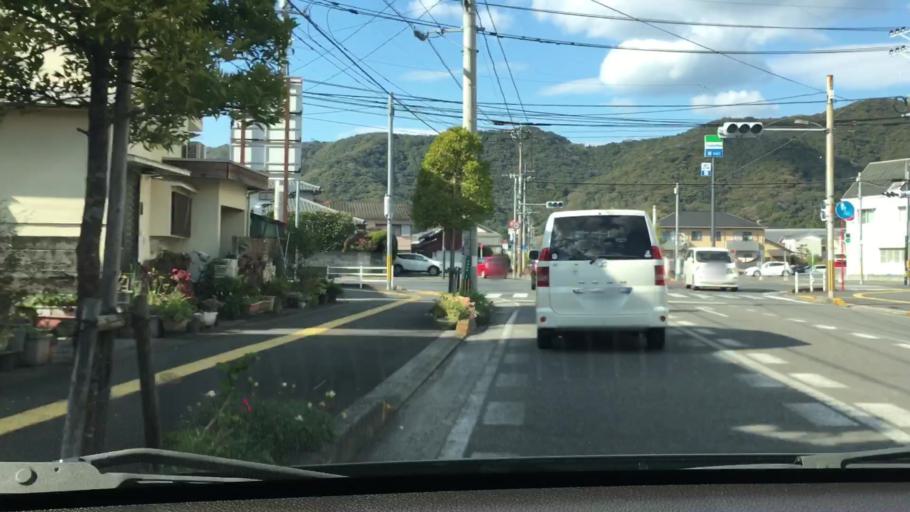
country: JP
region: Oita
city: Saiki
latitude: 32.9614
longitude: 131.8998
